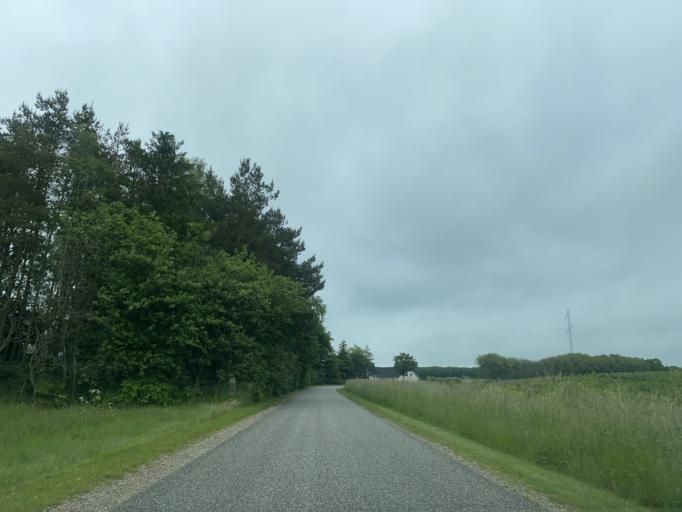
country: DK
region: Central Jutland
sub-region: Viborg Kommune
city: Bjerringbro
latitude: 56.3531
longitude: 9.6290
